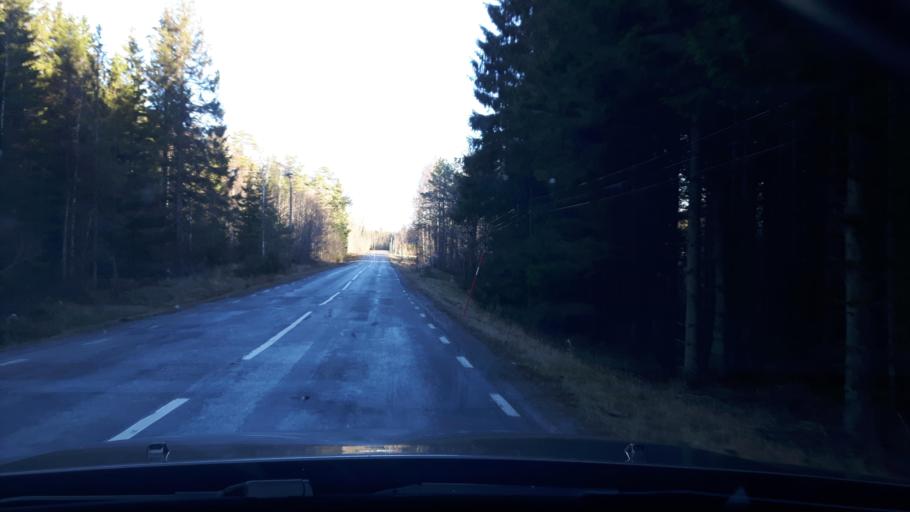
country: SE
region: Vaestra Goetaland
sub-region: Munkedals Kommun
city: Munkedal
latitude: 58.5254
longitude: 11.6890
